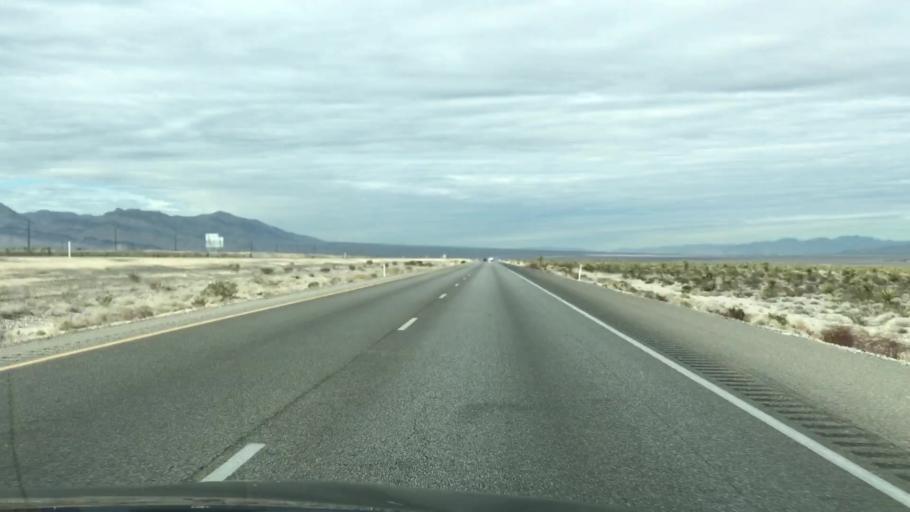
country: US
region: Nevada
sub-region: Clark County
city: Summerlin South
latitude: 36.3708
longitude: -115.3616
